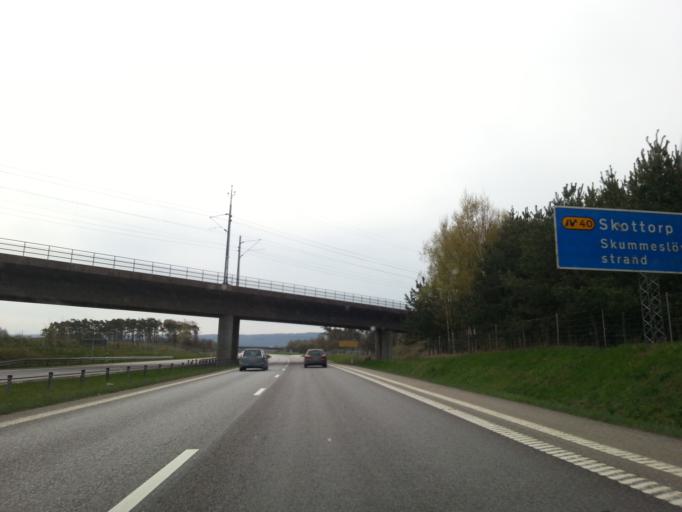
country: SE
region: Halland
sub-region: Laholms Kommun
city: Mellbystrand
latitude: 56.4581
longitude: 12.9438
